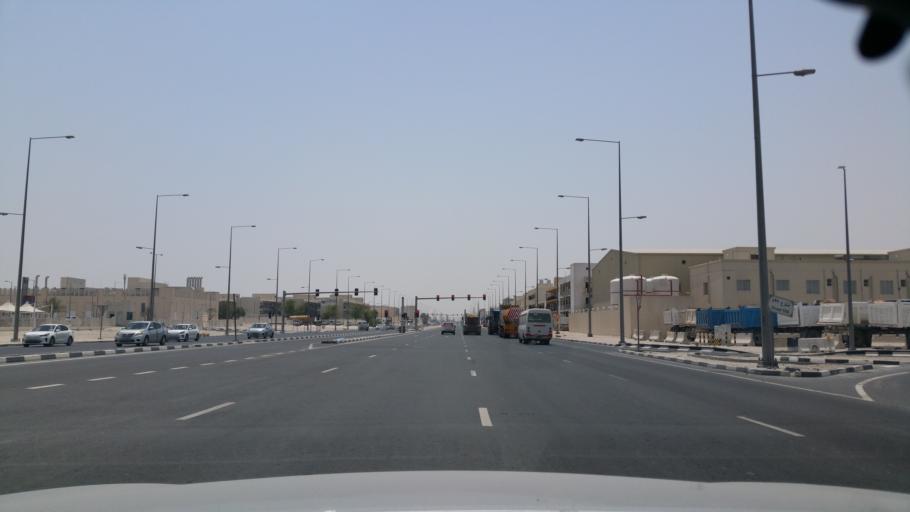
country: QA
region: Baladiyat ar Rayyan
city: Ar Rayyan
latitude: 25.1807
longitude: 51.4261
